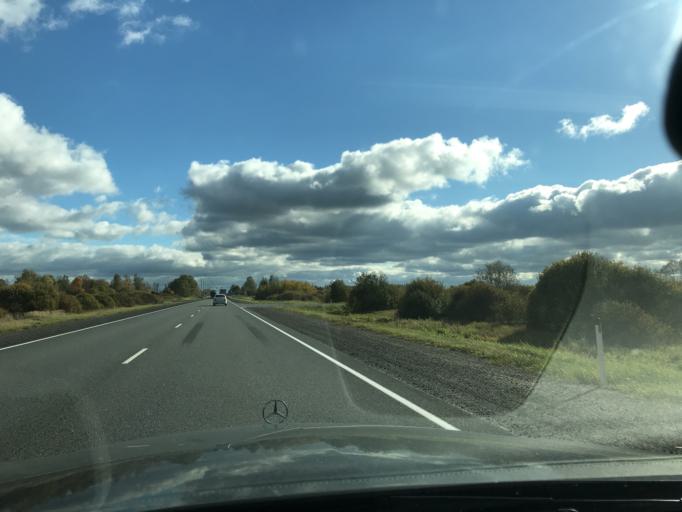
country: RU
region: Pskov
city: Ostrov
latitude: 57.1034
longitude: 28.5409
